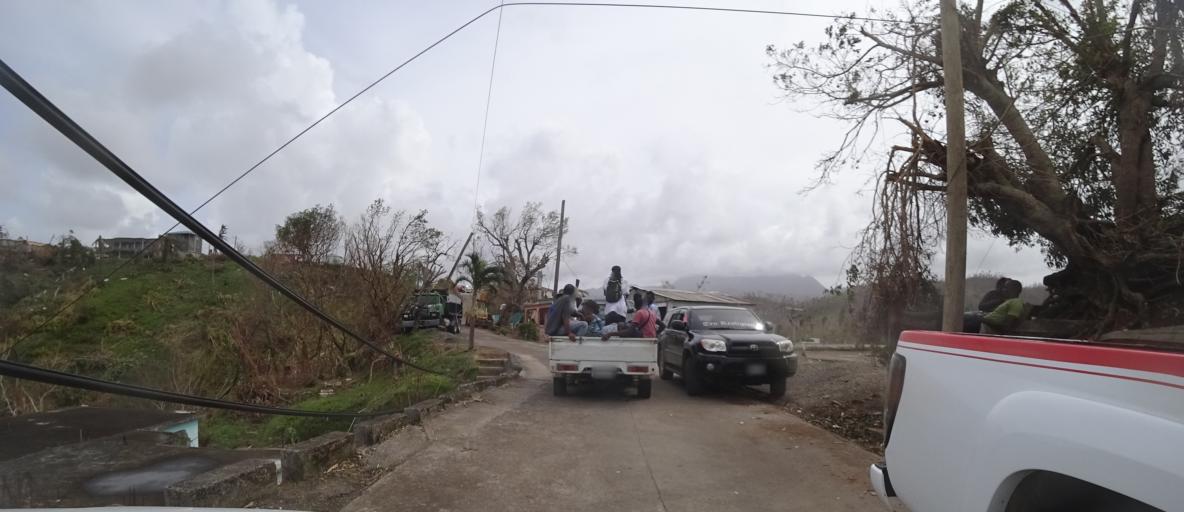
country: DM
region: Saint Andrew
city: Calibishie
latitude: 15.5865
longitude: -61.3748
